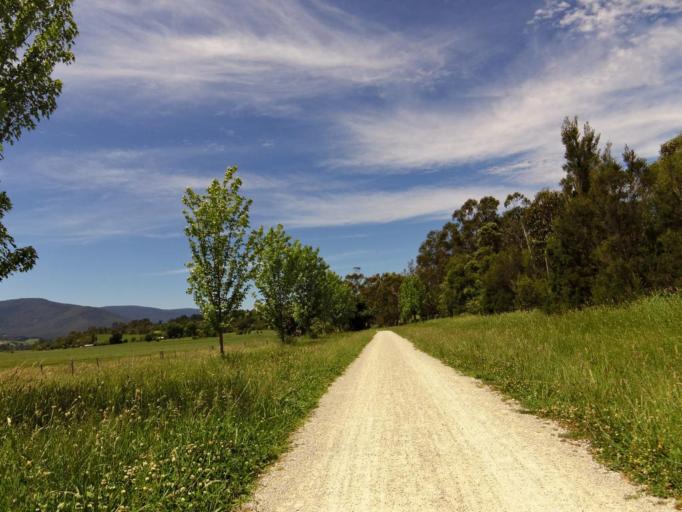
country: AU
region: Victoria
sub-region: Yarra Ranges
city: Woori Yallock
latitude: -37.7755
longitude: 145.5306
